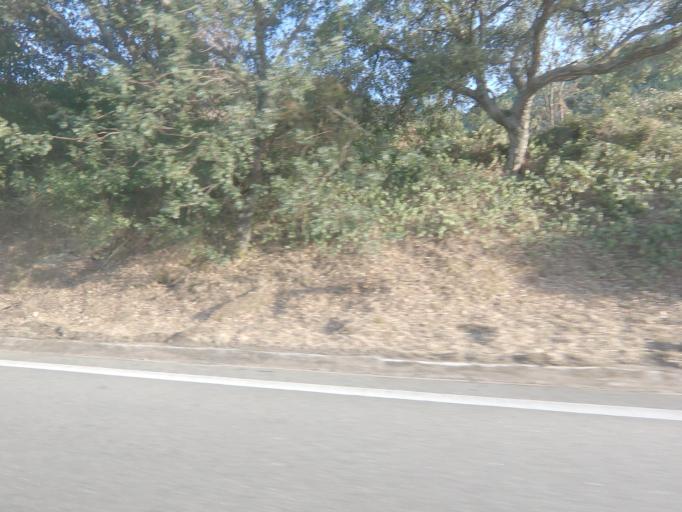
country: PT
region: Viseu
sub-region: Armamar
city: Armamar
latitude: 41.1611
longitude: -7.6560
